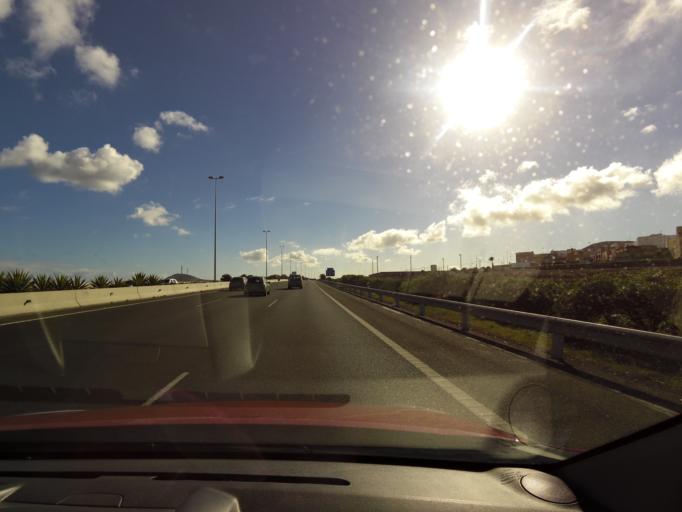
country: ES
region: Canary Islands
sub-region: Provincia de Las Palmas
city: Ingenio
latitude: 27.9110
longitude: -15.3994
